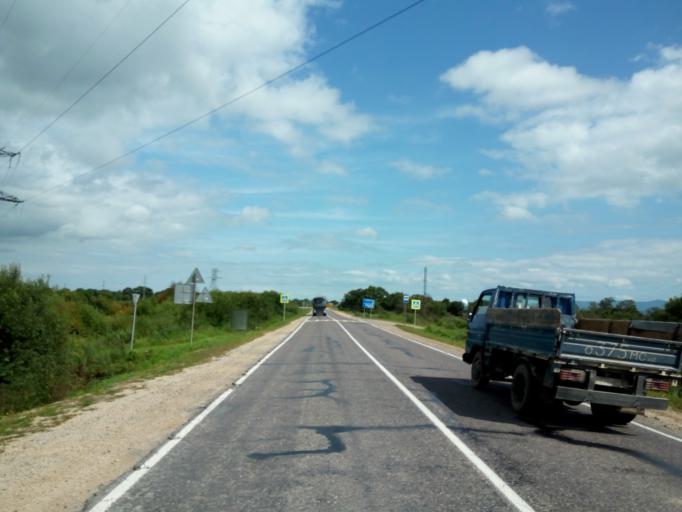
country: RU
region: Primorskiy
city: Dal'nerechensk
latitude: 45.9677
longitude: 133.7838
